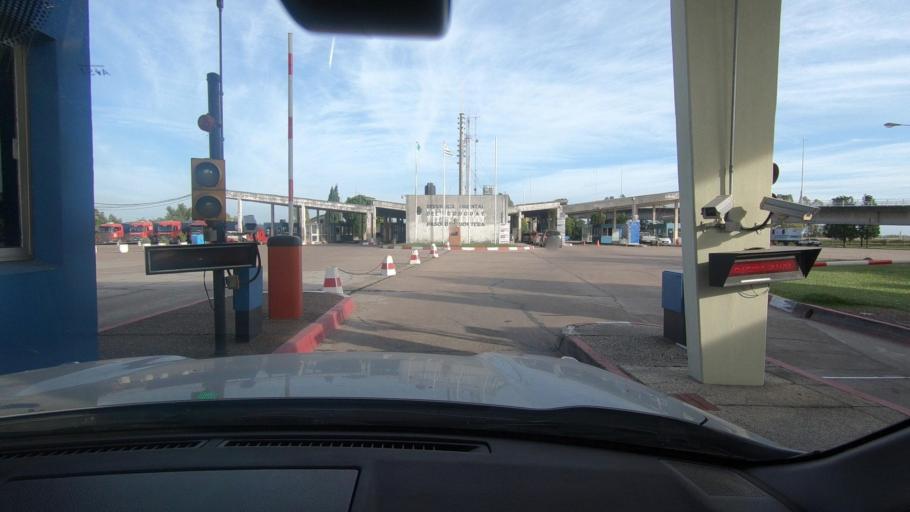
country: AR
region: Entre Rios
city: Colon
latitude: -32.2576
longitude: -58.1365
